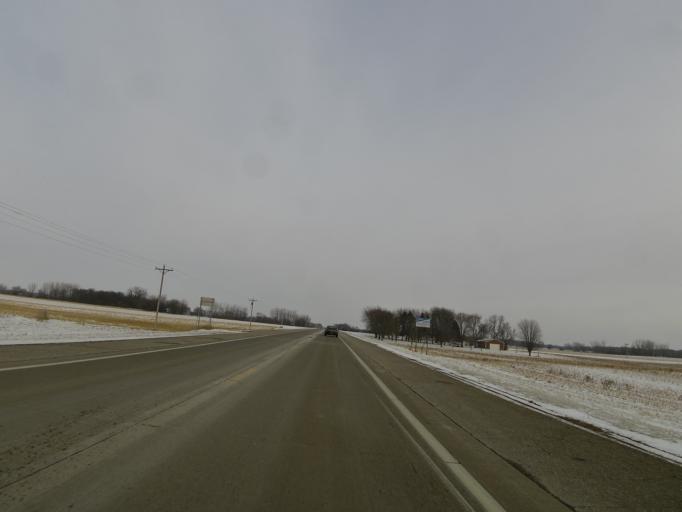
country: US
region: Minnesota
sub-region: McLeod County
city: Hutchinson
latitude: 44.8925
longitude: -94.3083
